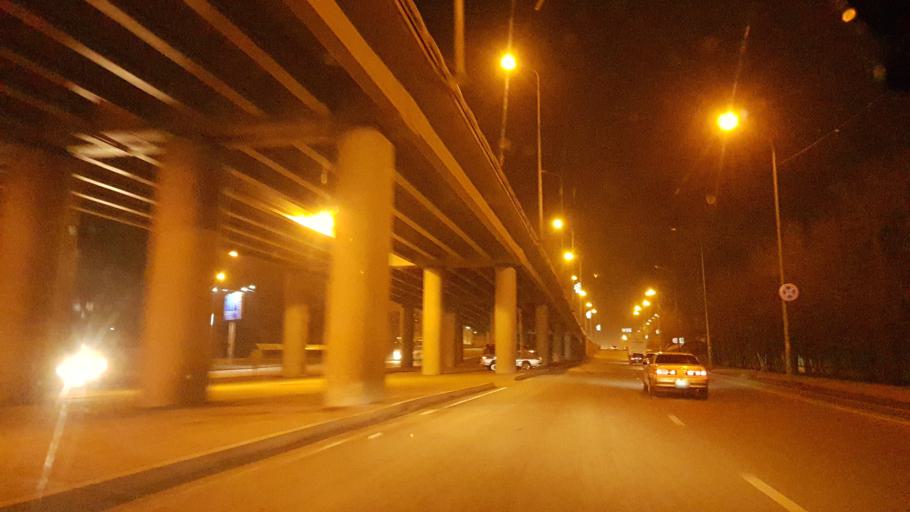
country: KZ
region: Almaty Qalasy
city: Almaty
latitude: 43.2722
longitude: 76.8856
